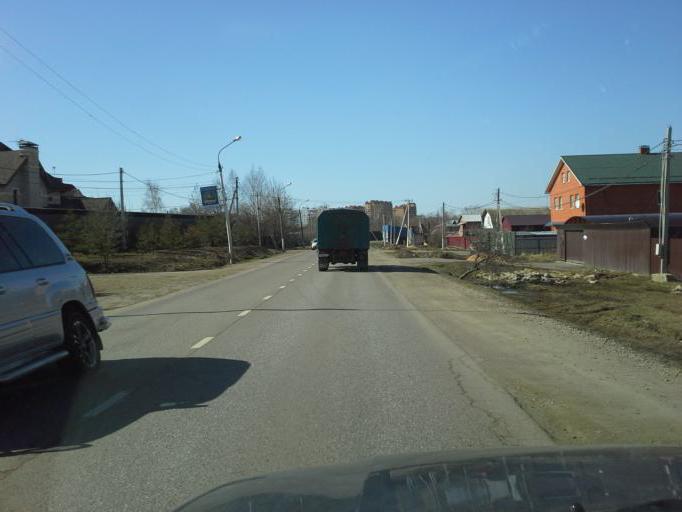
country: RU
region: Moscow
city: Vnukovo
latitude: 55.5954
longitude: 37.2142
